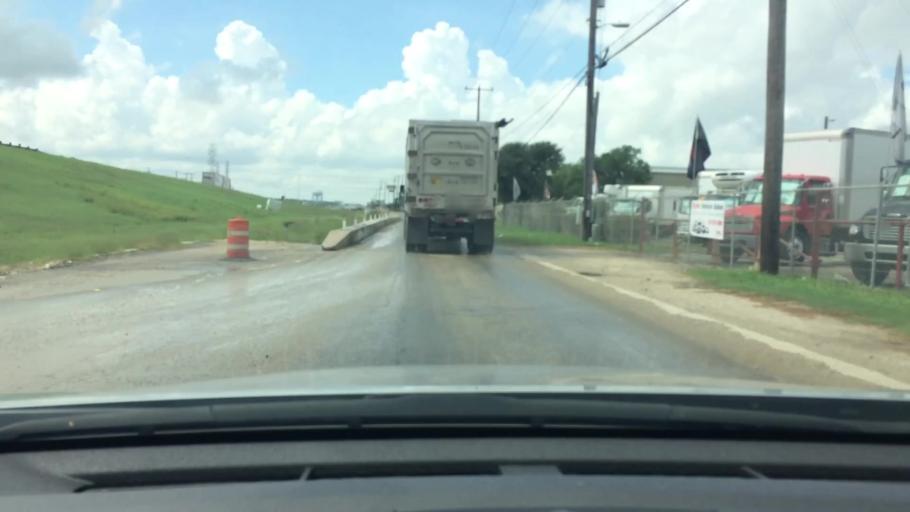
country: US
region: Texas
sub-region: Bexar County
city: Converse
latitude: 29.4592
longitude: -98.3175
